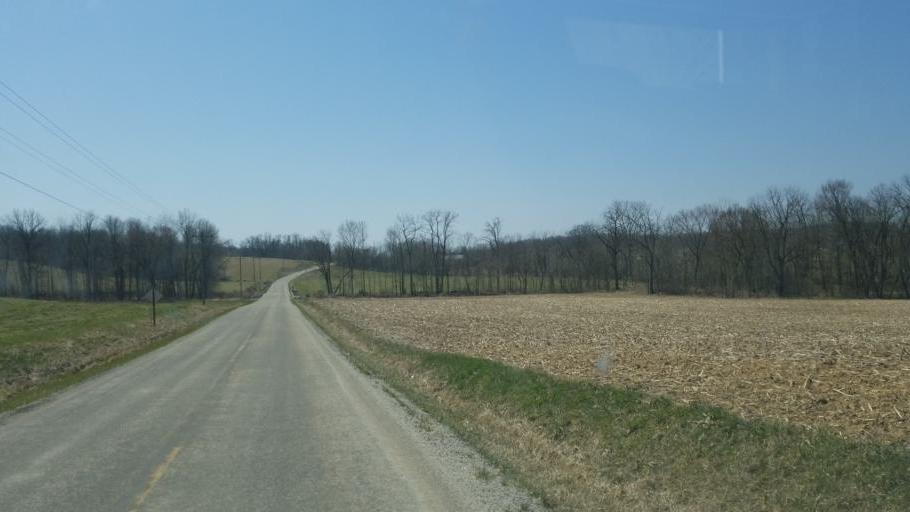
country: US
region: Ohio
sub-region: Ashland County
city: Loudonville
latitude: 40.7475
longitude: -82.2432
